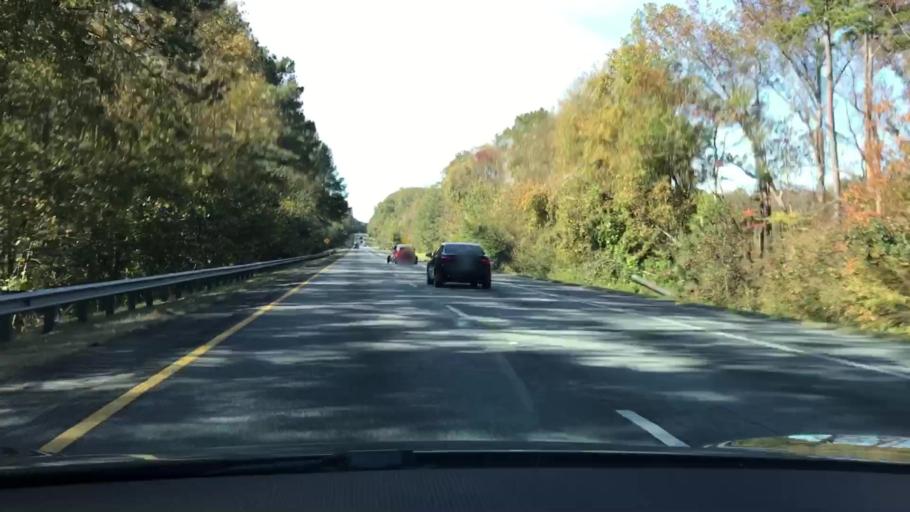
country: US
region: Georgia
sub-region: Morgan County
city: Madison
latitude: 33.5777
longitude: -83.5474
